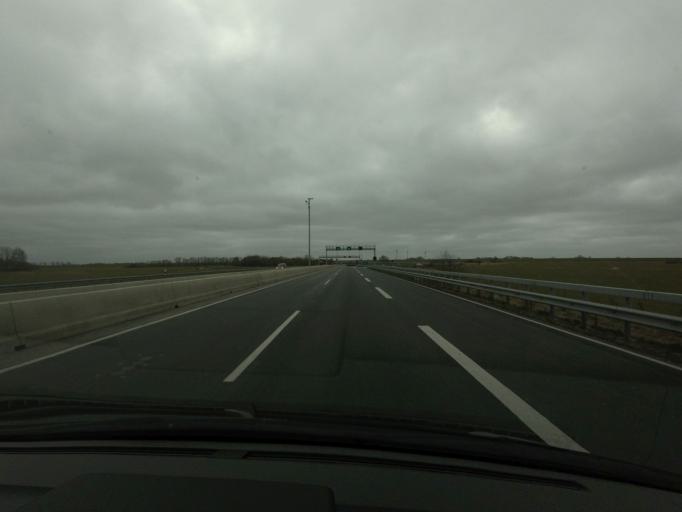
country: DE
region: Lower Saxony
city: Jemgum
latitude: 53.2400
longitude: 7.4151
